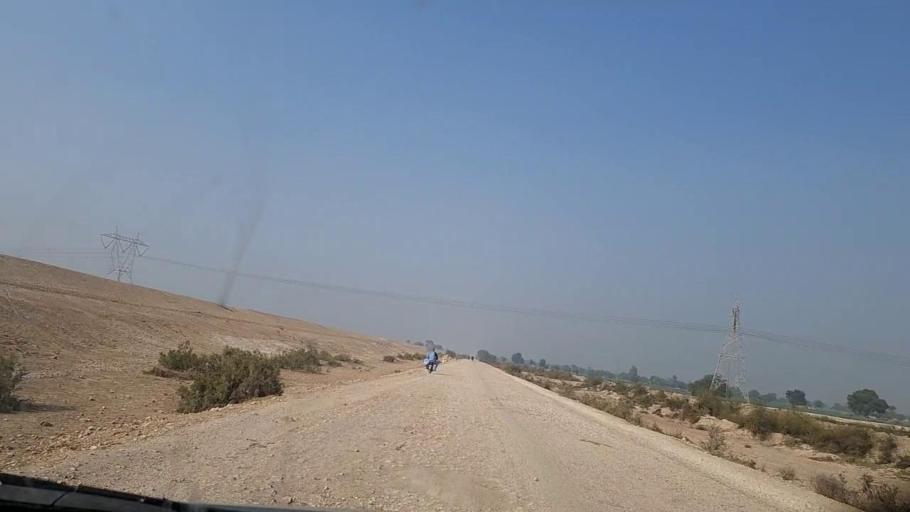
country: PK
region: Sindh
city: Moro
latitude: 26.7097
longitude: 67.9251
